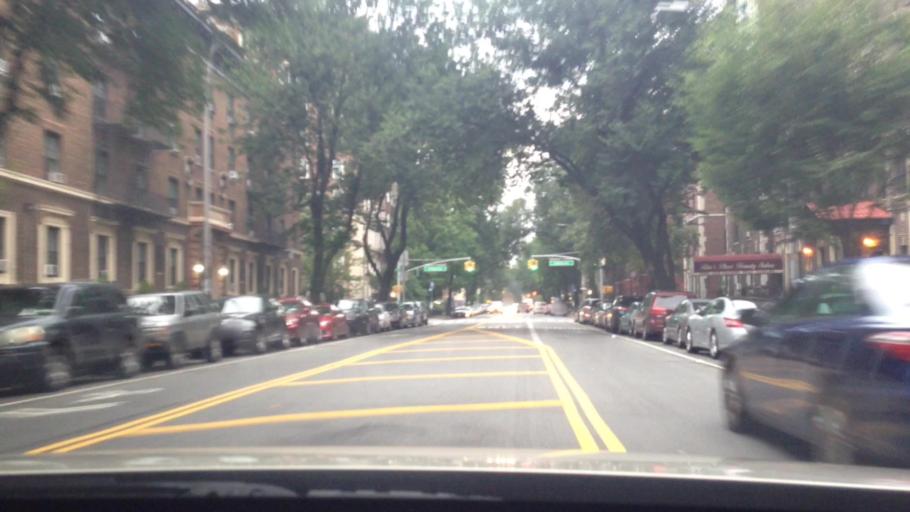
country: US
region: New York
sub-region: Kings County
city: Brooklyn
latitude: 40.6513
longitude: -73.9613
